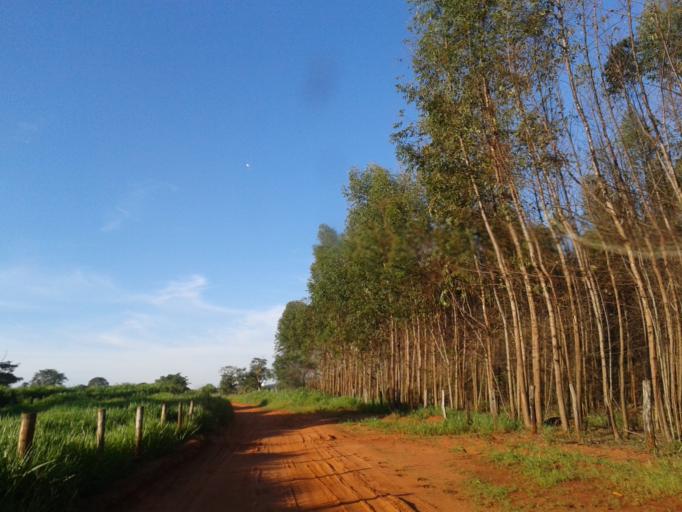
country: BR
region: Minas Gerais
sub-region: Santa Vitoria
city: Santa Vitoria
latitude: -18.9315
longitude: -49.8551
